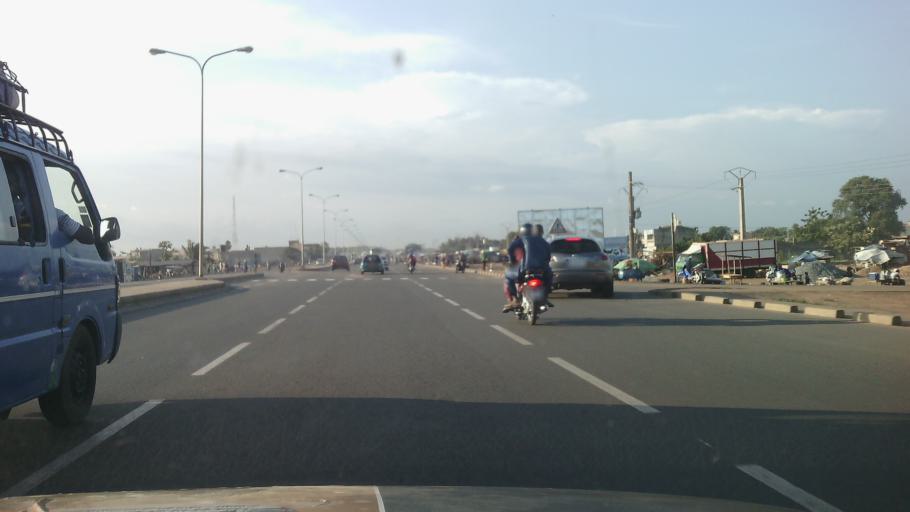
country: TG
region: Maritime
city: Lome
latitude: 6.2481
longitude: 1.2094
